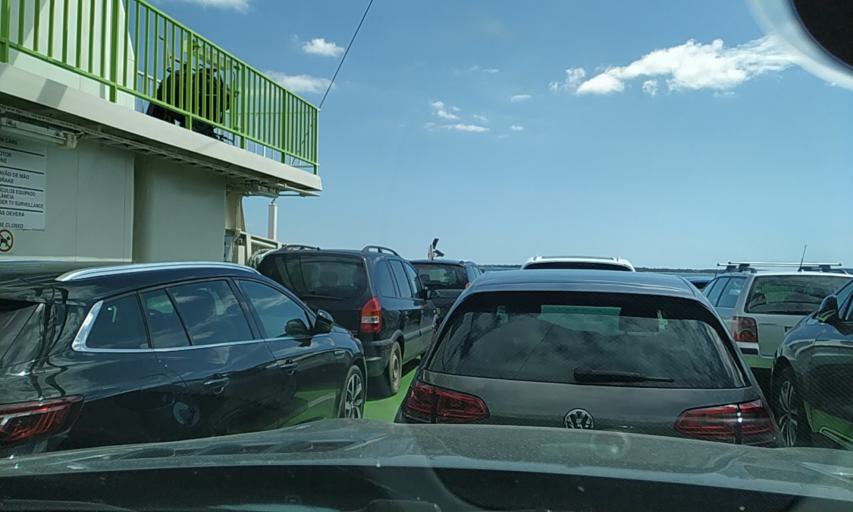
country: PT
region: Setubal
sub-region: Setubal
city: Setubal
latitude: 38.5162
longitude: -8.8857
